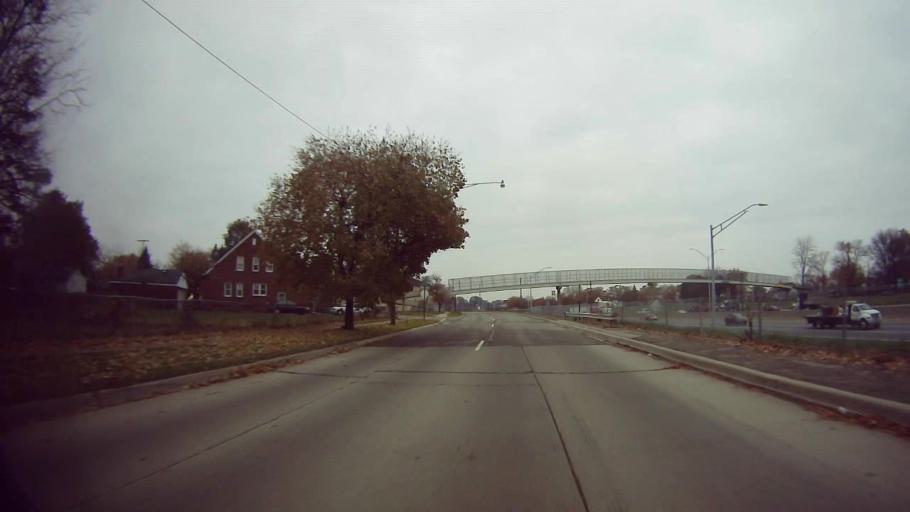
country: US
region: Michigan
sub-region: Oakland County
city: Hazel Park
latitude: 42.4575
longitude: -83.0991
